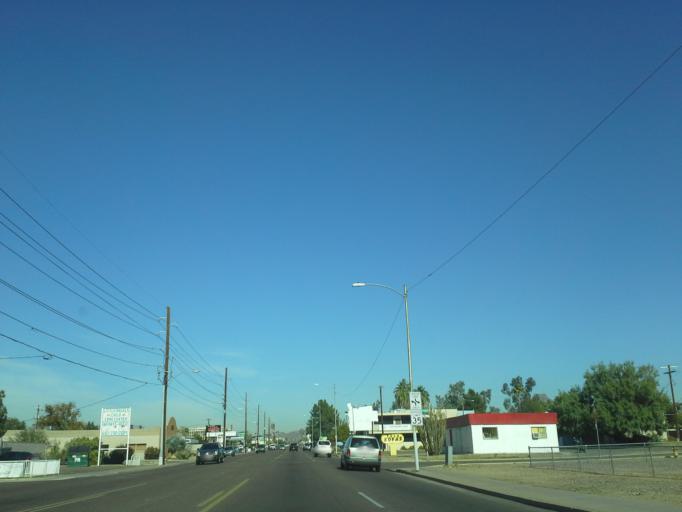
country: US
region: Arizona
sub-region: Maricopa County
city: Phoenix
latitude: 33.4884
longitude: -112.0476
